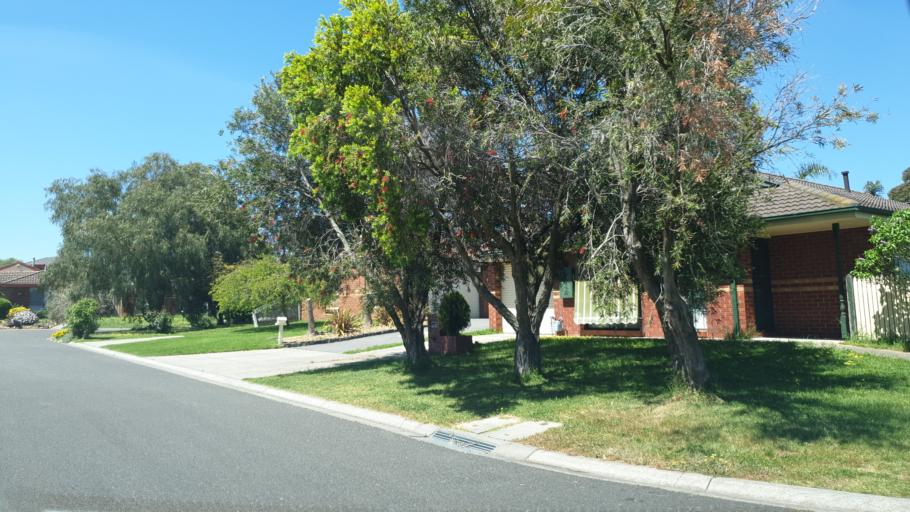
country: AU
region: Victoria
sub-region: Casey
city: Cranbourne North
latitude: -38.0820
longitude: 145.2841
